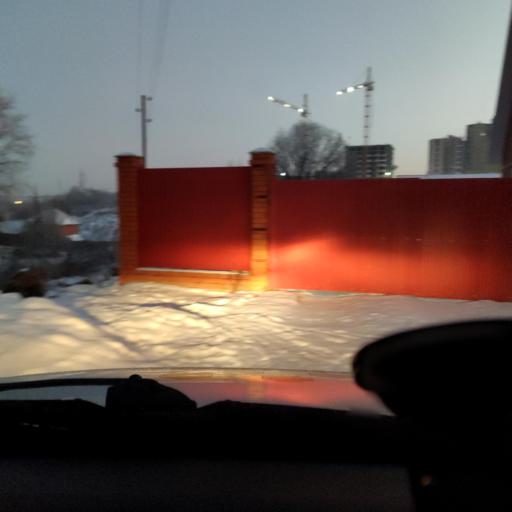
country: RU
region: Perm
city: Perm
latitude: 58.0098
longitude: 56.3261
